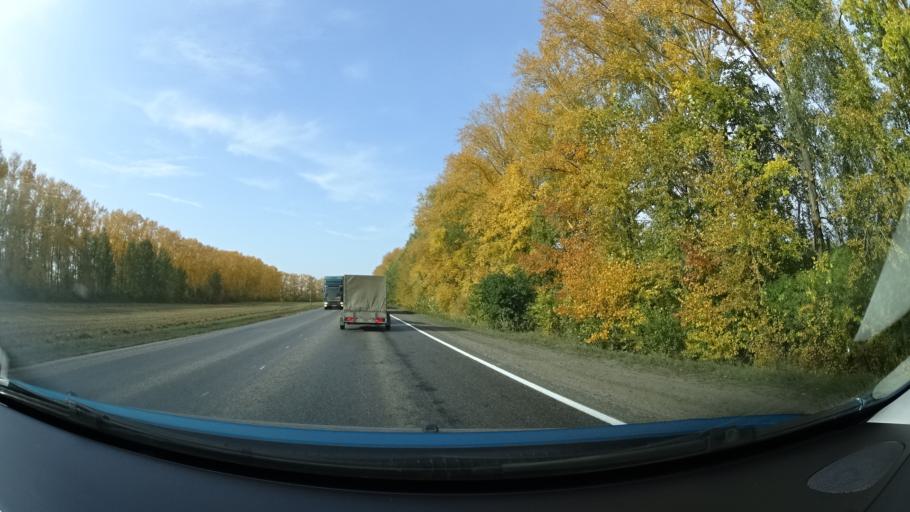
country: RU
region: Bashkortostan
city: Buzdyak
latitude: 54.6185
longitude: 54.3870
